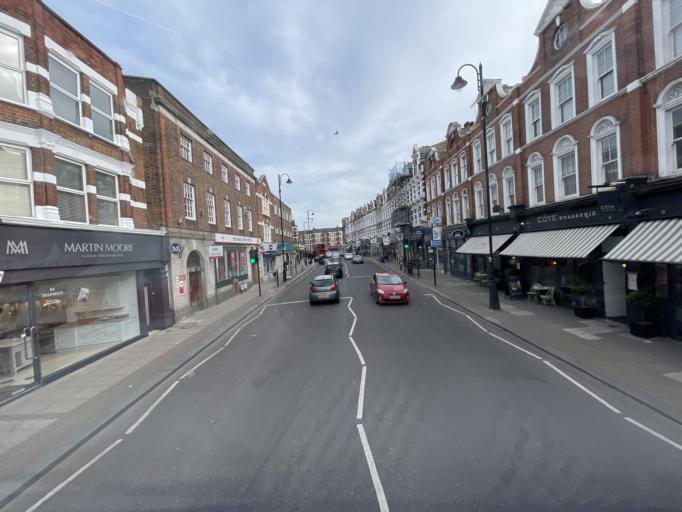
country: GB
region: England
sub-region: Greater London
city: Crouch End
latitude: 51.5923
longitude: -0.1432
